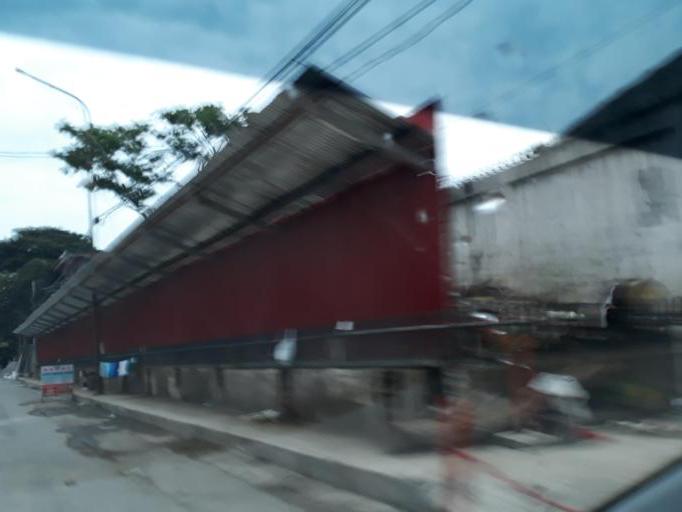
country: PH
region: Calabarzon
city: Del Monte
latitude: 14.6288
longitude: 121.0036
